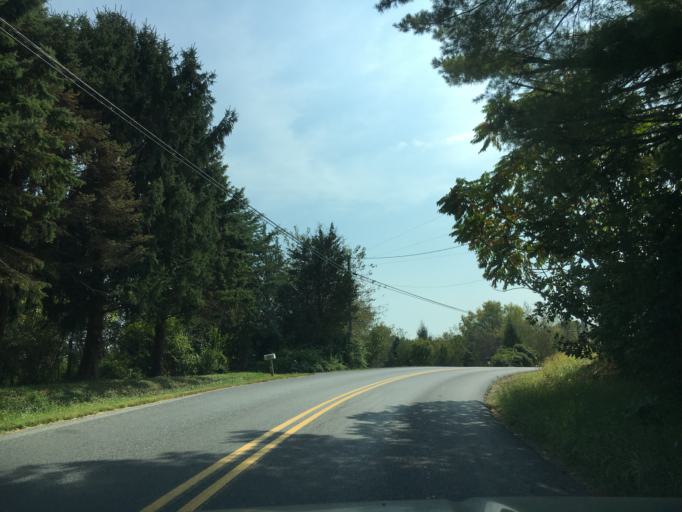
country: US
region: Pennsylvania
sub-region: Berks County
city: Topton
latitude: 40.5725
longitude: -75.7077
